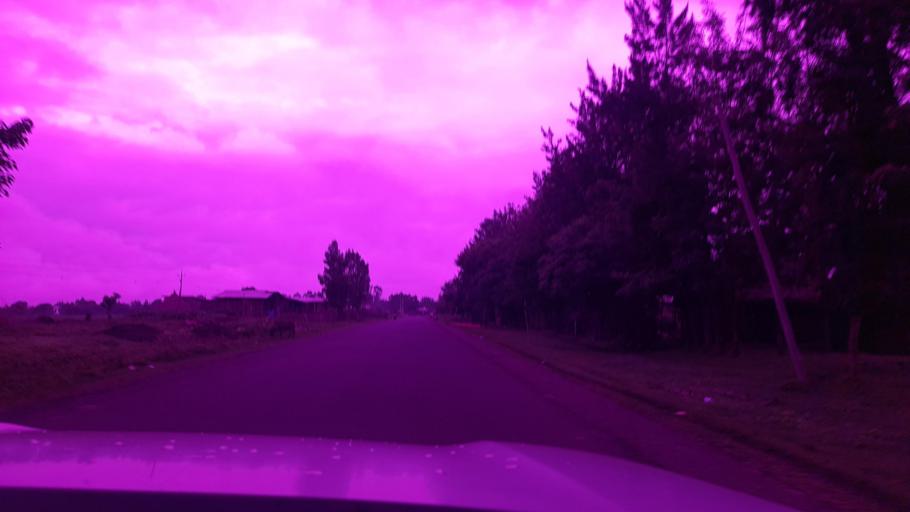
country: ET
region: Oromiya
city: Waliso
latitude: 8.2709
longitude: 37.6606
